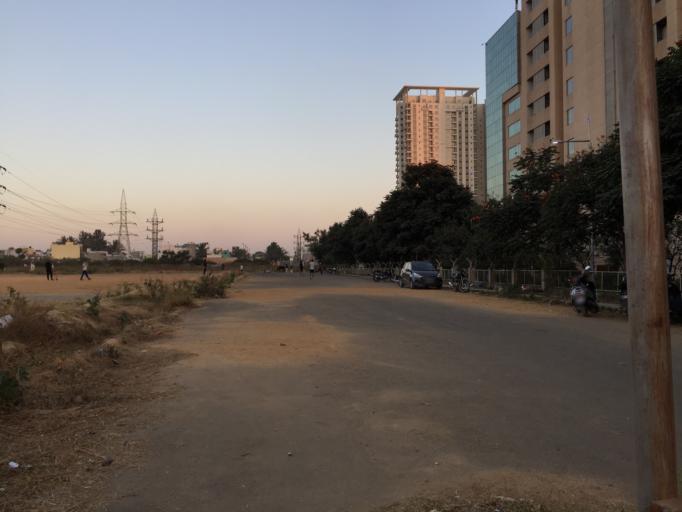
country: IN
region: Karnataka
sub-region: Bangalore Urban
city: Yelahanka
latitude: 13.0509
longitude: 77.6231
